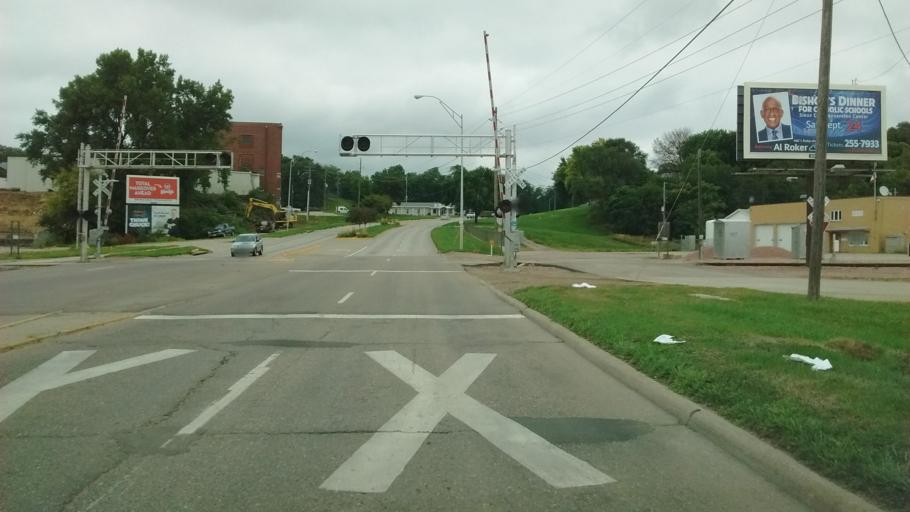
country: US
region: Nebraska
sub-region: Dakota County
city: South Sioux City
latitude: 42.4949
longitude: -96.4241
